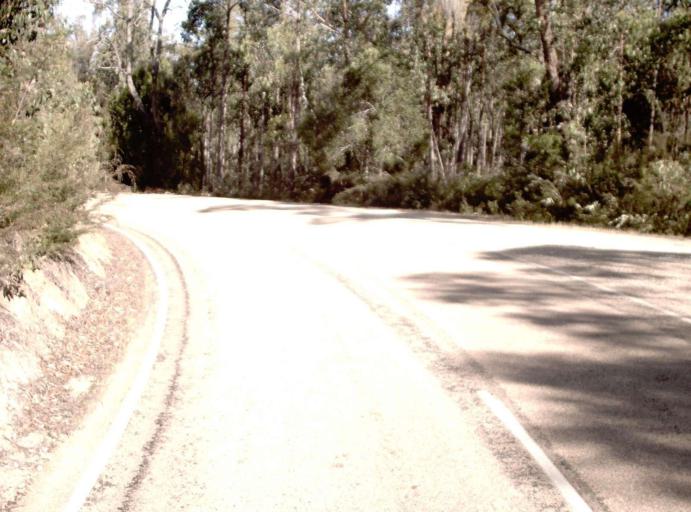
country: AU
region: Victoria
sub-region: East Gippsland
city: Lakes Entrance
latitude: -37.5465
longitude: 148.5546
